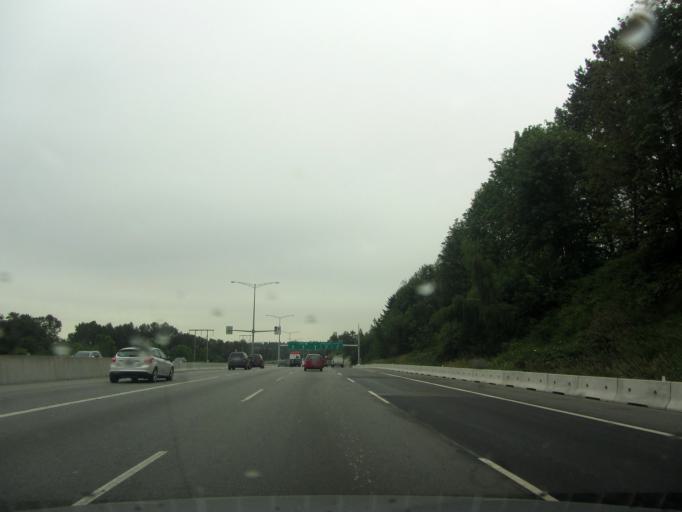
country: CA
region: British Columbia
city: Burnaby
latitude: 49.2576
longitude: -123.0127
